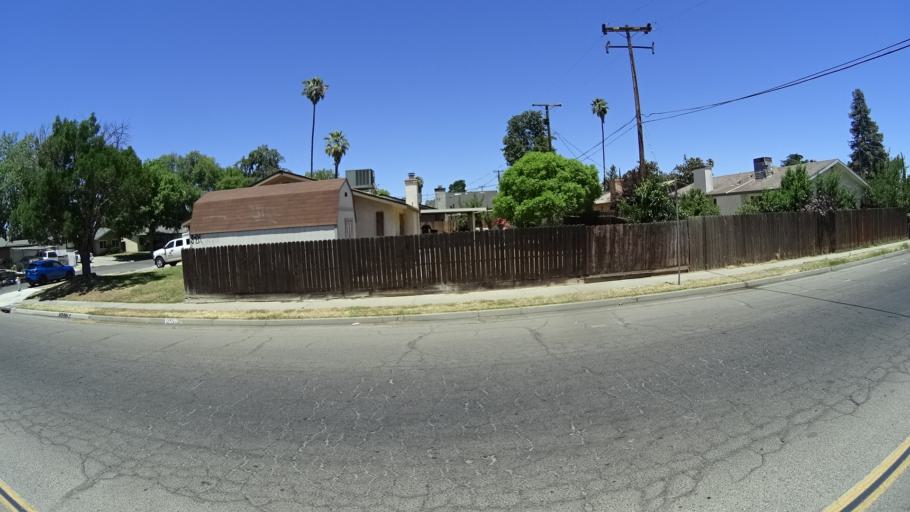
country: US
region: California
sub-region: Fresno County
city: West Park
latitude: 36.7865
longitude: -119.8429
